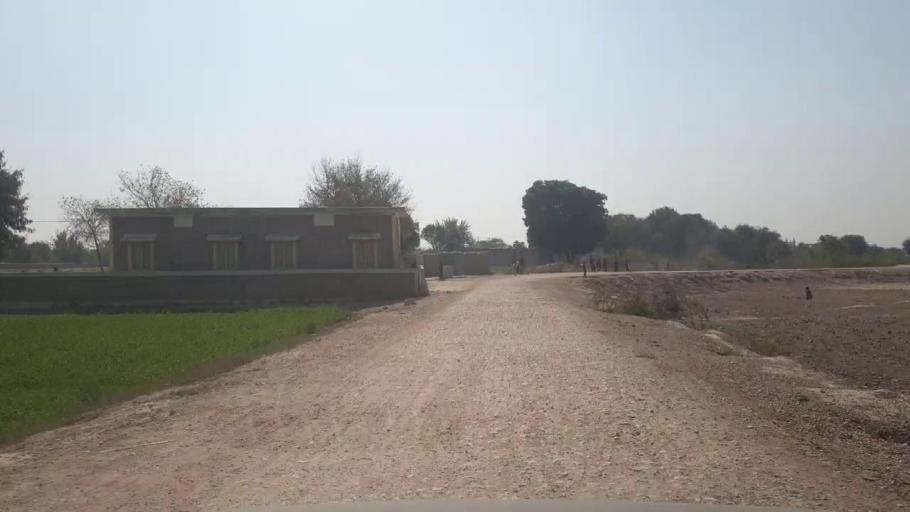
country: PK
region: Sindh
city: Chambar
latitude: 25.2335
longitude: 68.8235
